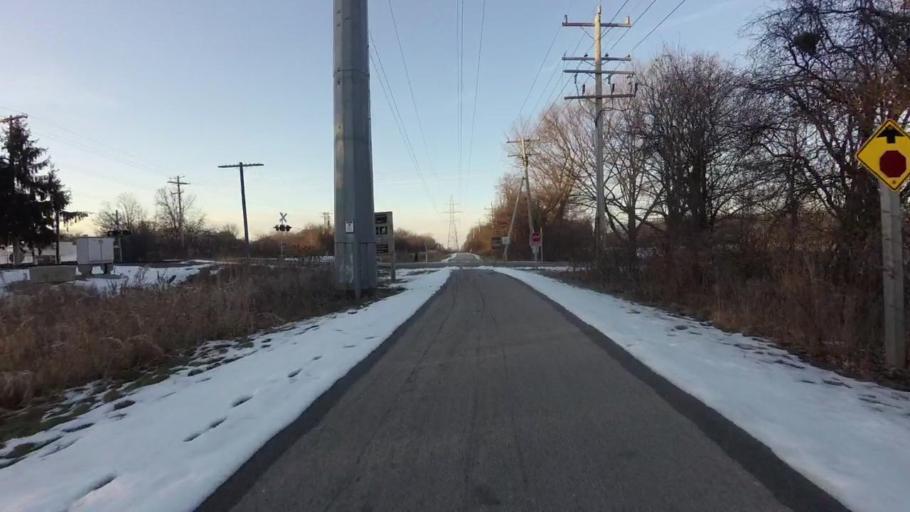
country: US
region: Wisconsin
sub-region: Milwaukee County
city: Brown Deer
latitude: 43.1556
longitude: -87.9576
